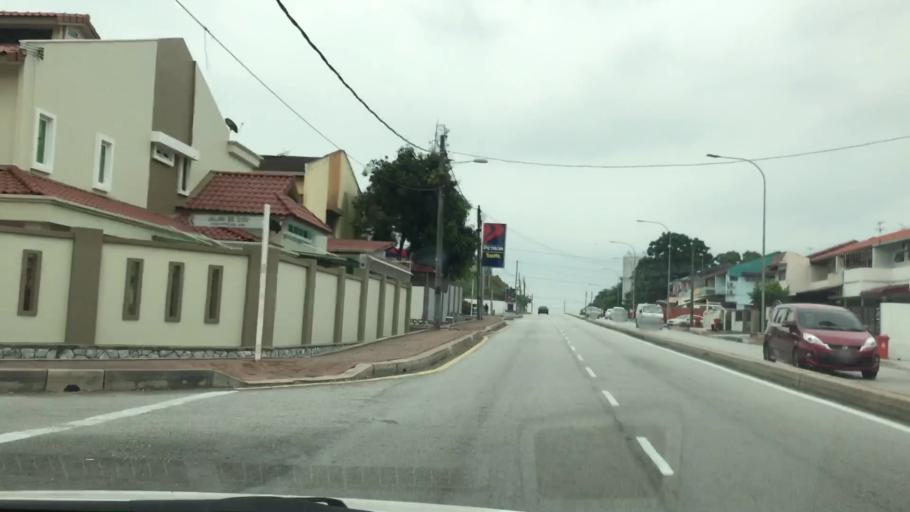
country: MY
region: Selangor
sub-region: Petaling
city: Petaling Jaya
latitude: 3.1125
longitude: 101.6196
